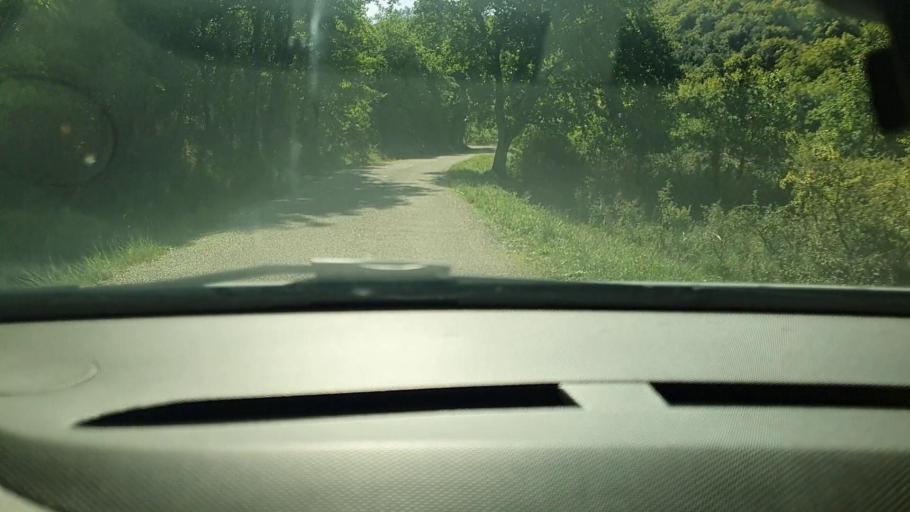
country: FR
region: Languedoc-Roussillon
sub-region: Departement du Gard
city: Saint-Ambroix
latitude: 44.2222
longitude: 4.2859
